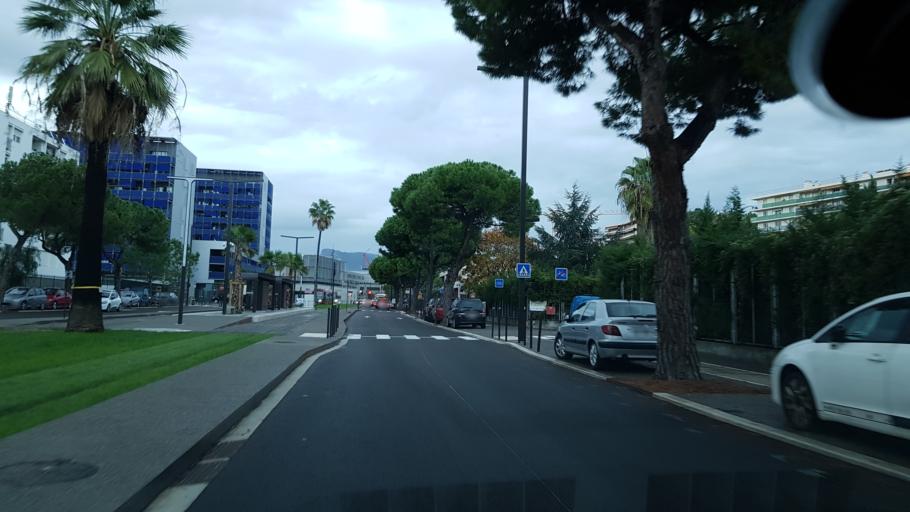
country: FR
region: Provence-Alpes-Cote d'Azur
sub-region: Departement des Alpes-Maritimes
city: Saint-Laurent-du-Var
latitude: 43.6762
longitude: 7.2065
